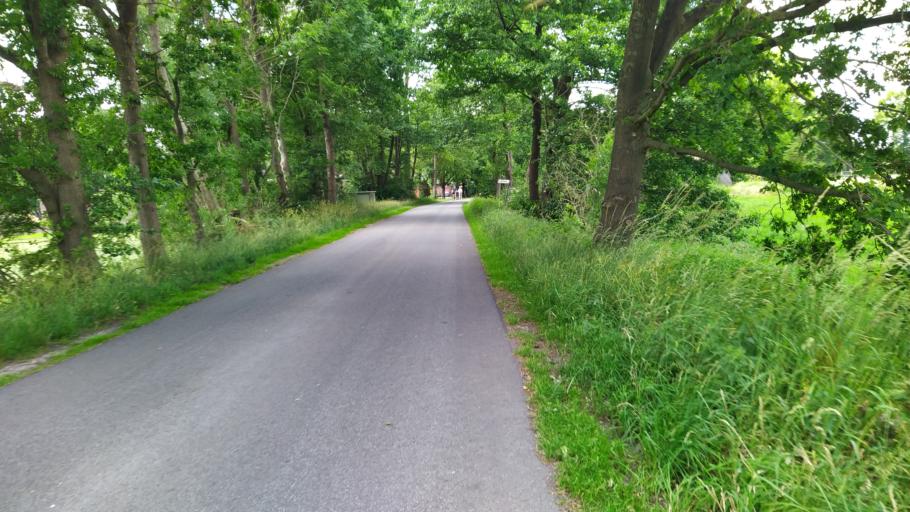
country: DE
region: Lower Saxony
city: Hollnseth
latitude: 53.5733
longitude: 9.1151
